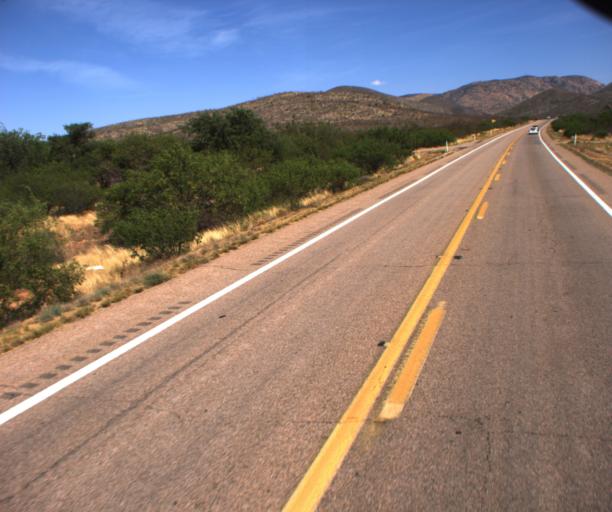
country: US
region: Arizona
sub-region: Cochise County
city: Bisbee
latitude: 31.5251
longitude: -110.0459
